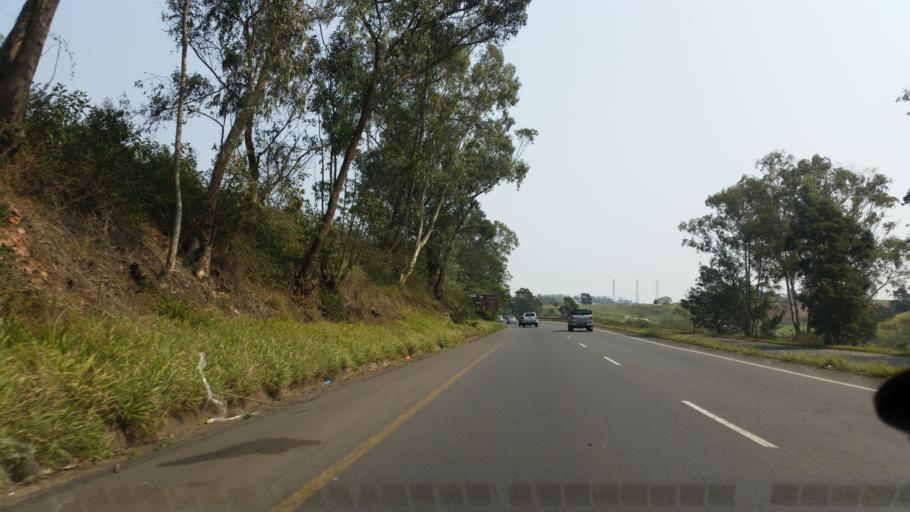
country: ZA
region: KwaZulu-Natal
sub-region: eThekwini Metropolitan Municipality
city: Mpumalanga
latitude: -29.7965
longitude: 30.7499
